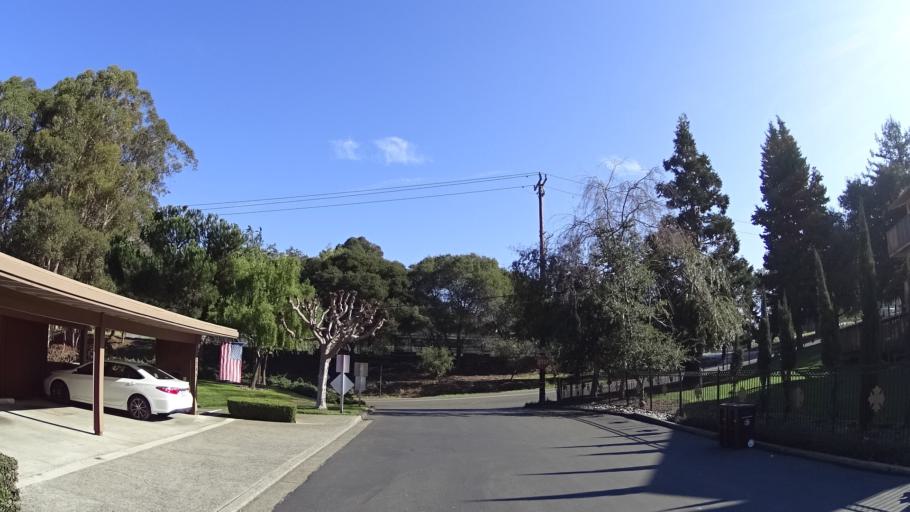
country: US
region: California
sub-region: Alameda County
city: Fairview
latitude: 37.6731
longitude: -122.0563
